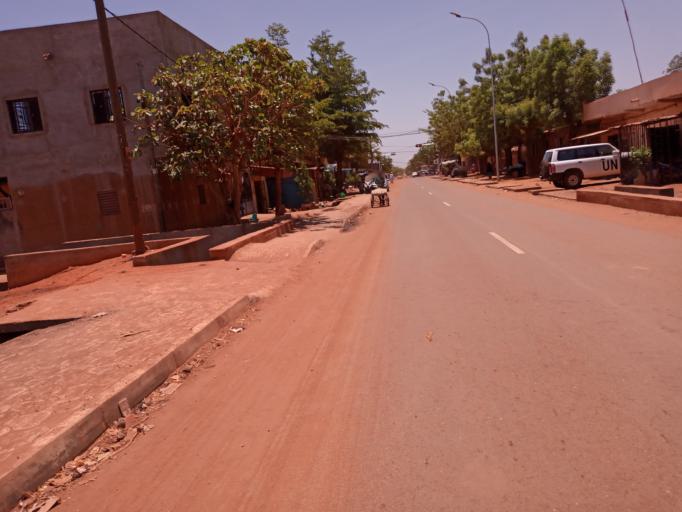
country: ML
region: Bamako
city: Bamako
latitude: 12.5899
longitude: -7.9827
